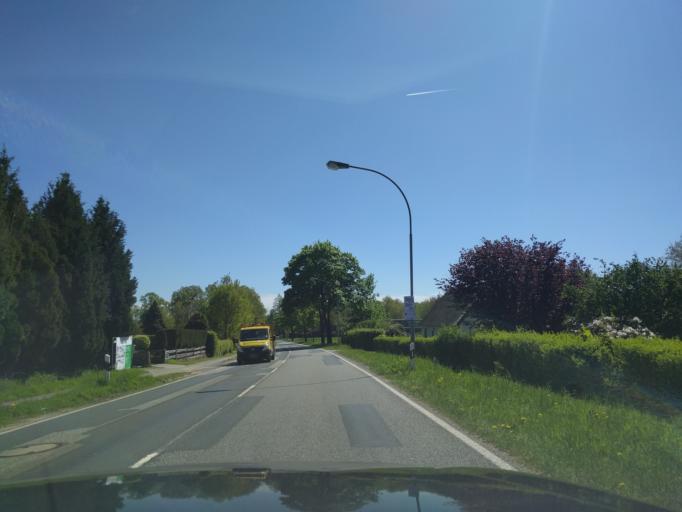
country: DE
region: Lower Saxony
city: Seevetal
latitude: 53.4040
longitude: 10.0022
